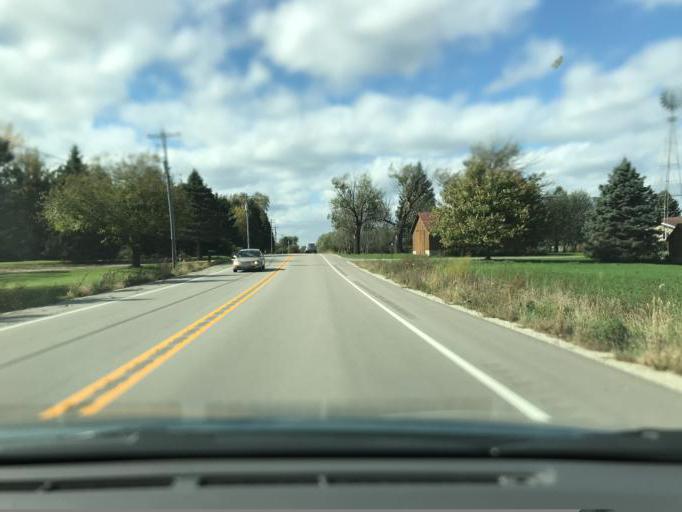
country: US
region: Wisconsin
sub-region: Racine County
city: Browns Lake
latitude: 42.6524
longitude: -88.2136
